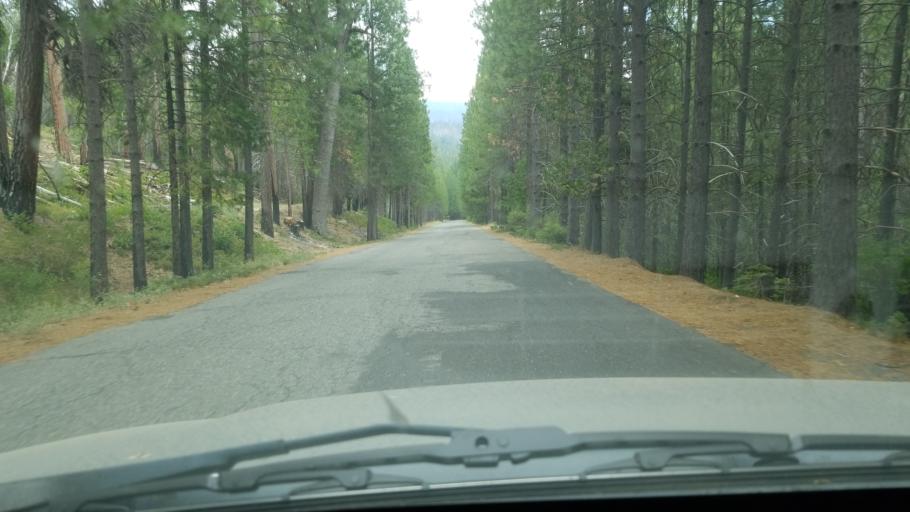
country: US
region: California
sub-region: Mariposa County
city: Midpines
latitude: 37.8178
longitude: -119.8664
